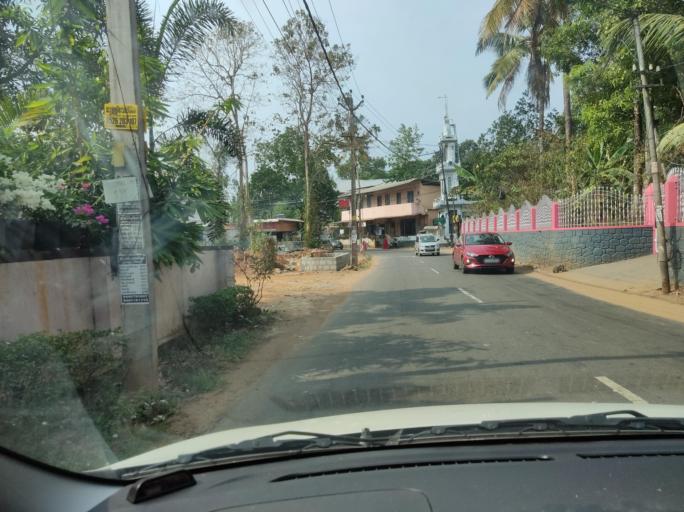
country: IN
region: Kerala
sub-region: Kottayam
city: Kottayam
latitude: 9.6850
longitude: 76.5056
